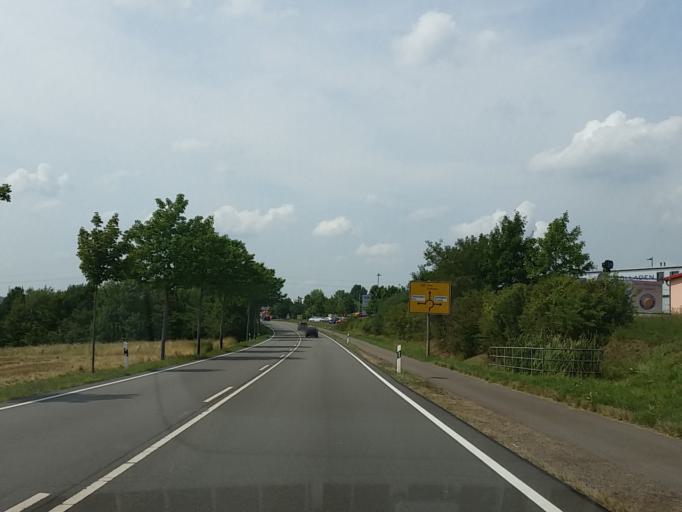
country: DE
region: Saarland
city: Schmelz
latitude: 49.4386
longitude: 6.8762
